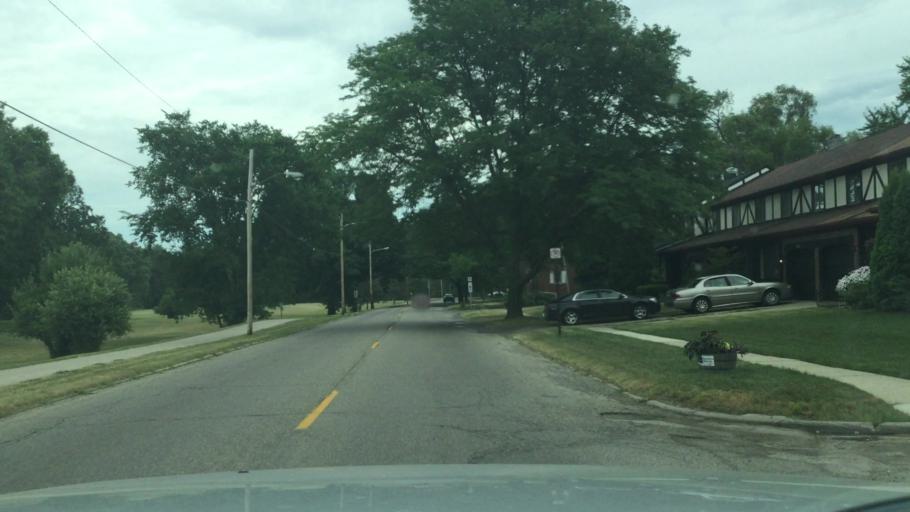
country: US
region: Michigan
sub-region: Genesee County
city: Flint
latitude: 43.0130
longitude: -83.7260
